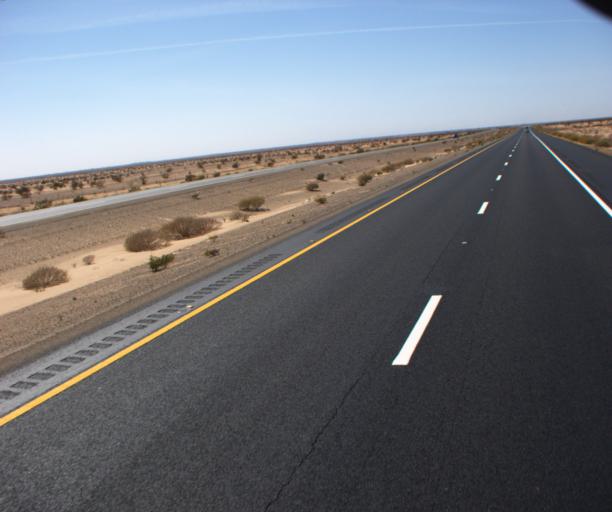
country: US
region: Arizona
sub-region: Yuma County
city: Somerton
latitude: 32.4953
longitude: -114.5813
